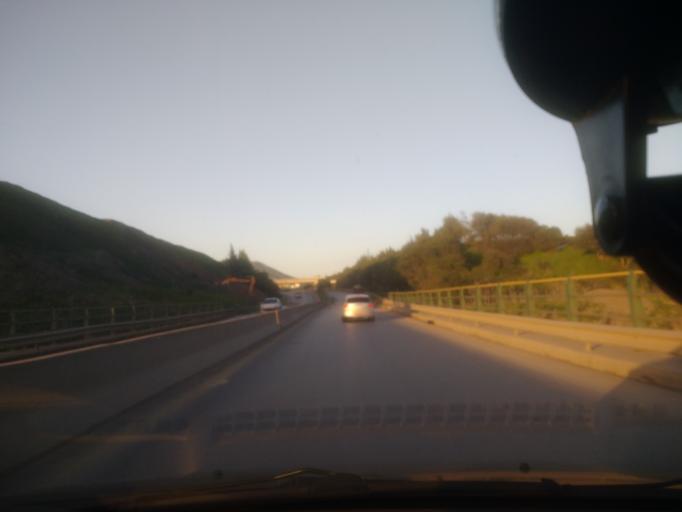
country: DZ
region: Tizi Ouzou
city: Tizi Ouzou
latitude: 36.7503
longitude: 4.0299
